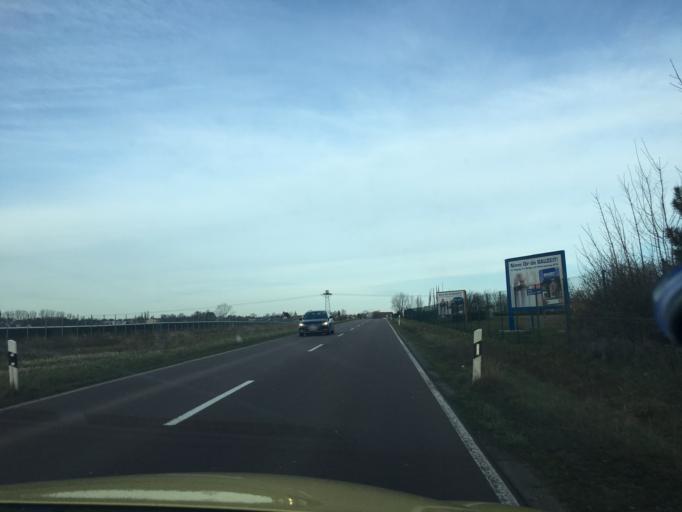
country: DE
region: Saxony-Anhalt
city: Reichardtswerben
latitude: 51.2484
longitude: 11.9738
